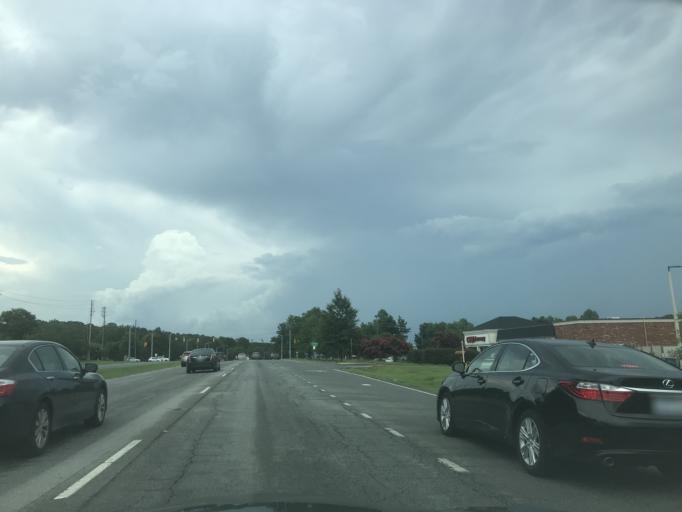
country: US
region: North Carolina
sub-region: Johnston County
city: Clayton
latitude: 35.6576
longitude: -78.4804
